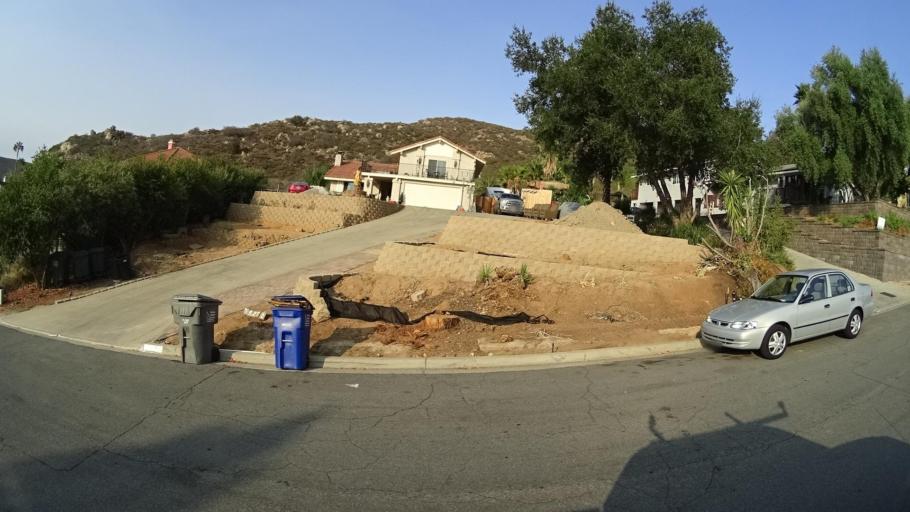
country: US
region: California
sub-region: San Diego County
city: San Diego Country Estates
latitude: 33.0106
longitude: -116.8258
